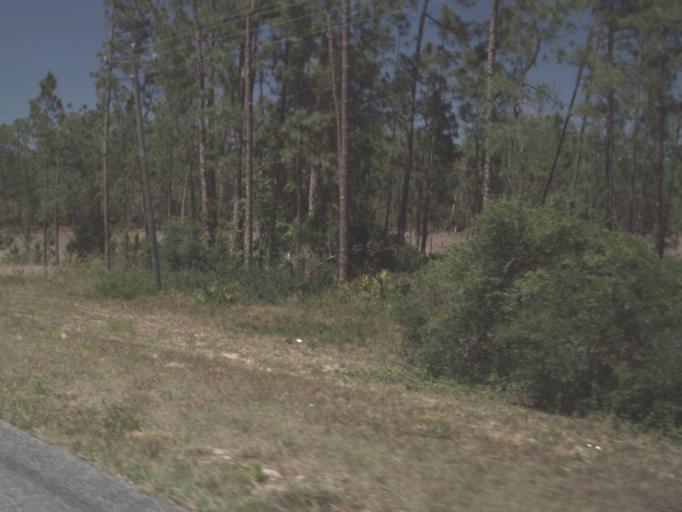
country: US
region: Florida
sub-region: Lake County
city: Astor
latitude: 29.1397
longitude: -81.6278
